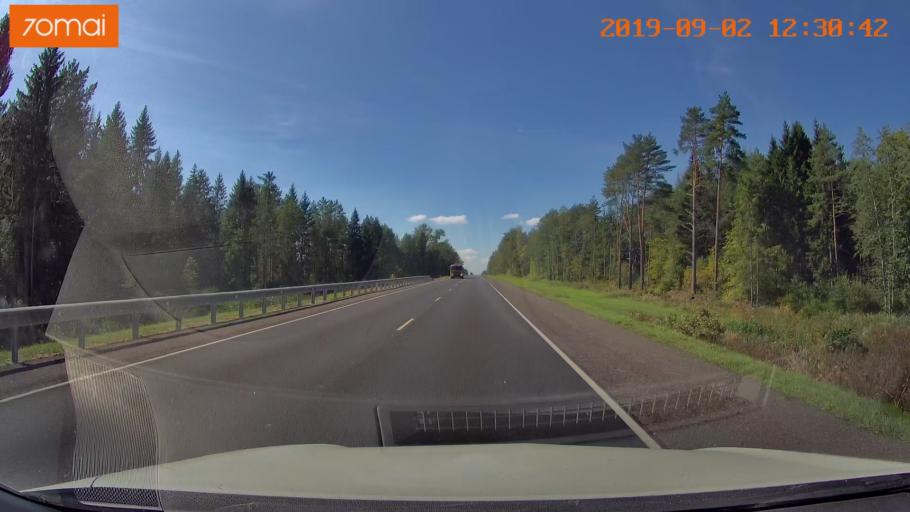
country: RU
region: Smolensk
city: Shumyachi
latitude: 53.8300
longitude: 32.4678
